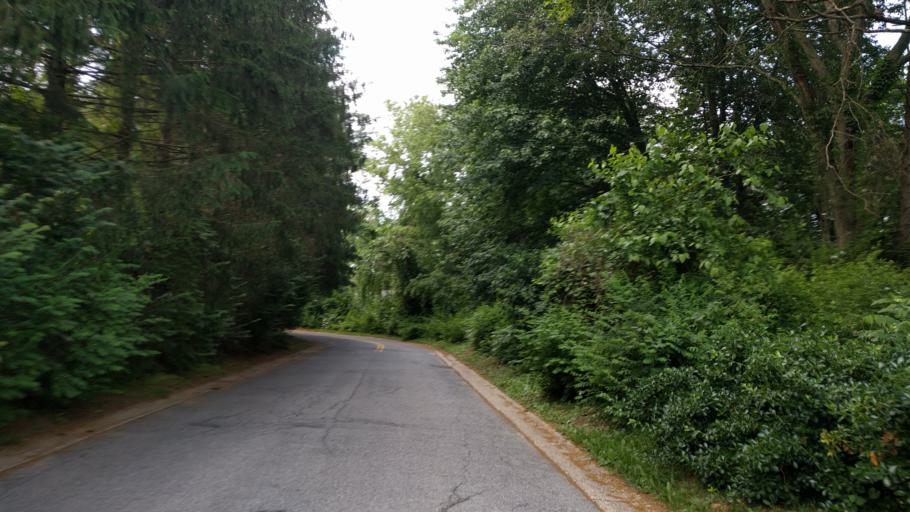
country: US
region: New York
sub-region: Nassau County
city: Old Brookville
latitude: 40.8470
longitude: -73.6071
